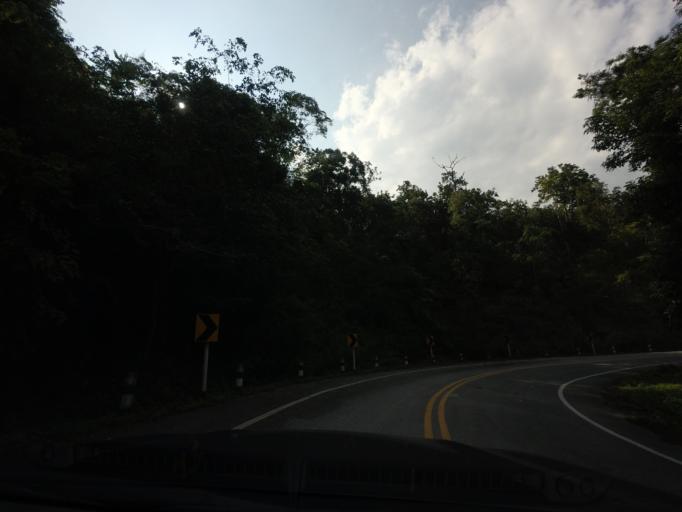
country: TH
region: Nan
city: Na Noi
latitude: 18.2747
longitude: 100.9677
